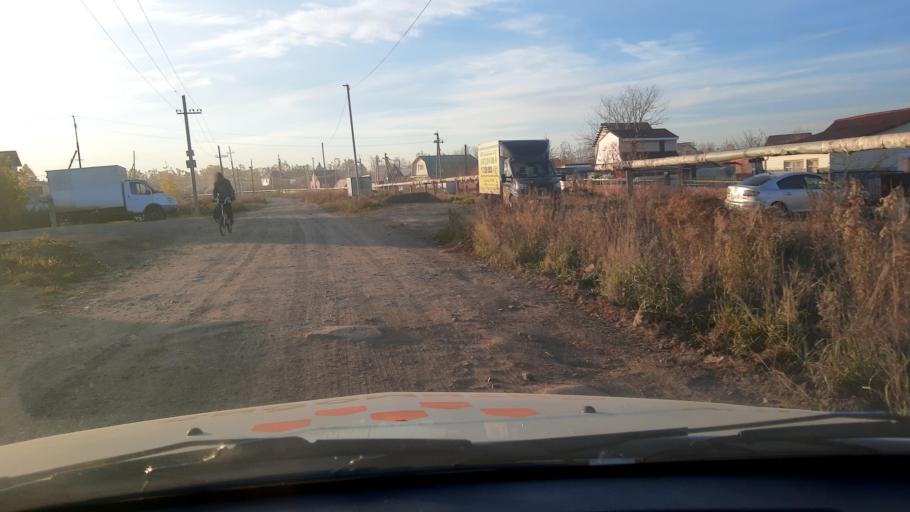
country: RU
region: Bashkortostan
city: Ufa
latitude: 54.8143
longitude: 56.1551
